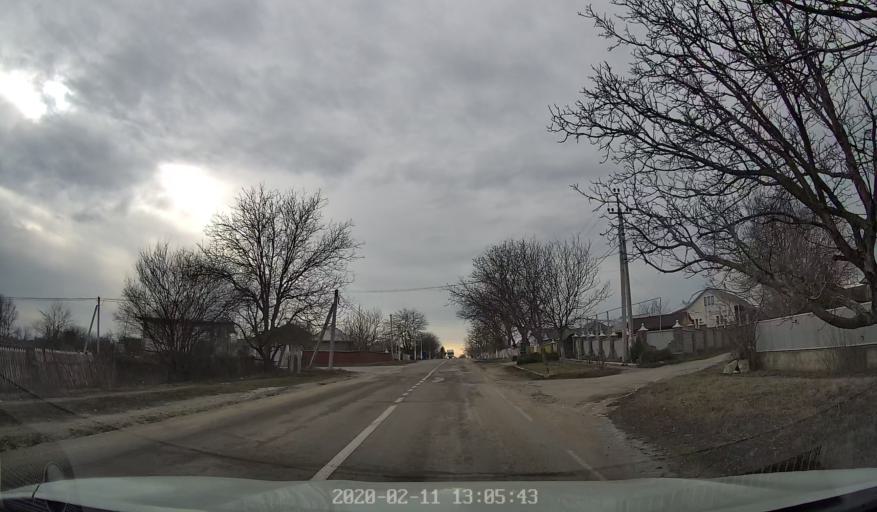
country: RO
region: Botosani
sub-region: Comuna Radauti-Prut
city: Miorcani
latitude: 48.2949
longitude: 26.9307
